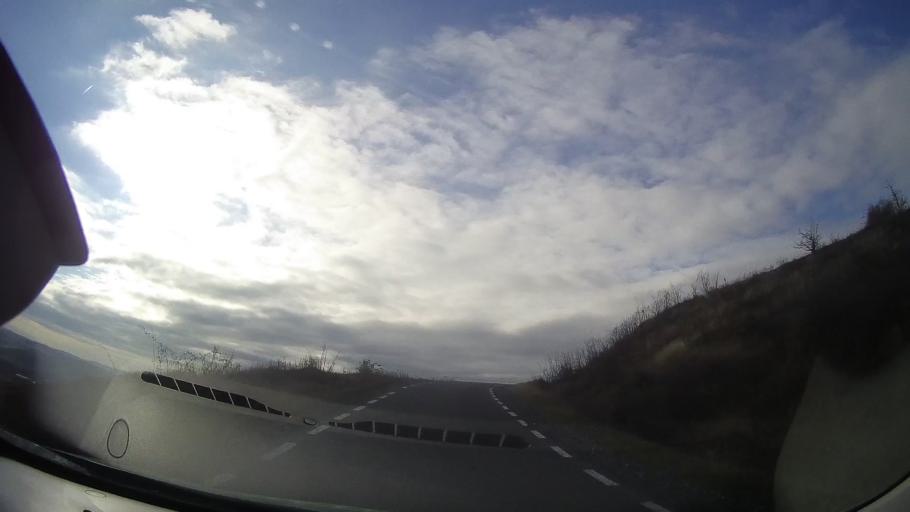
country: RO
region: Mures
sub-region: Comuna Sanger
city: Sanger
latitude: 46.5515
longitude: 24.1604
